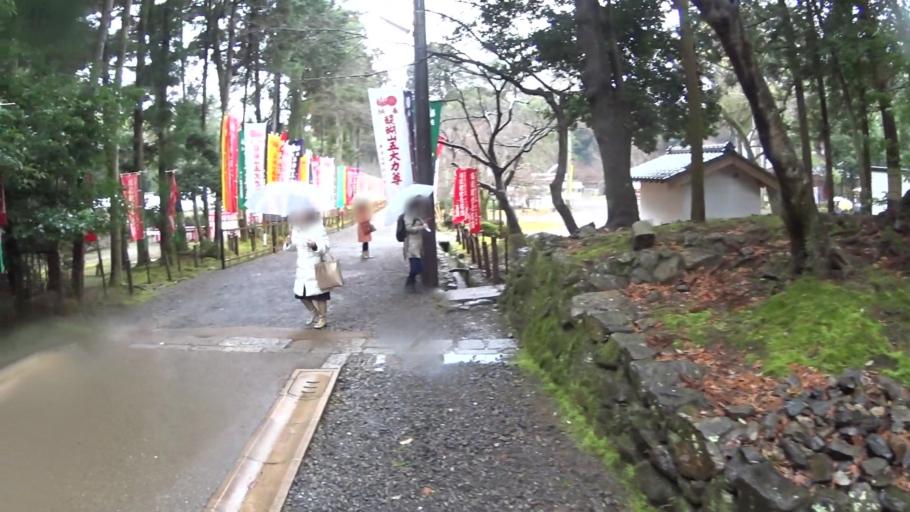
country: JP
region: Shiga Prefecture
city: Otsu-shi
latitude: 34.9556
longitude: 135.8221
